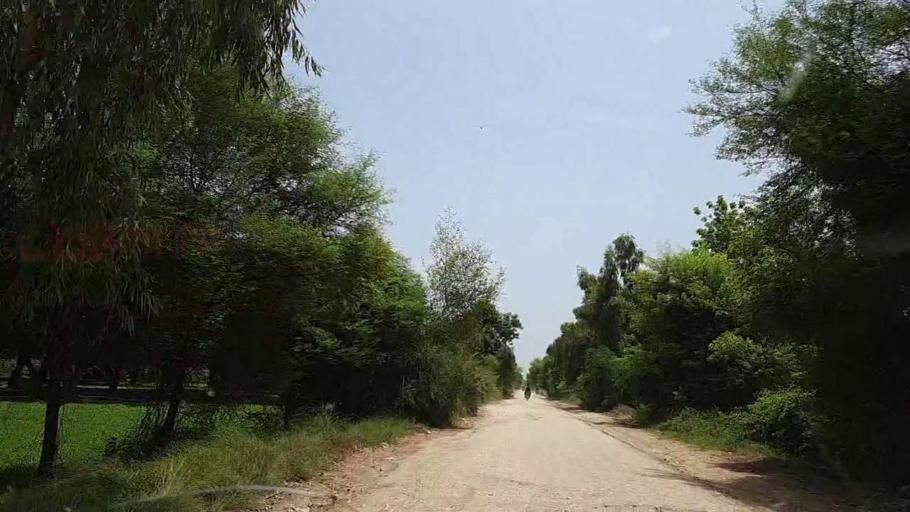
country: PK
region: Sindh
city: Tharu Shah
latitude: 26.9675
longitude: 68.0437
